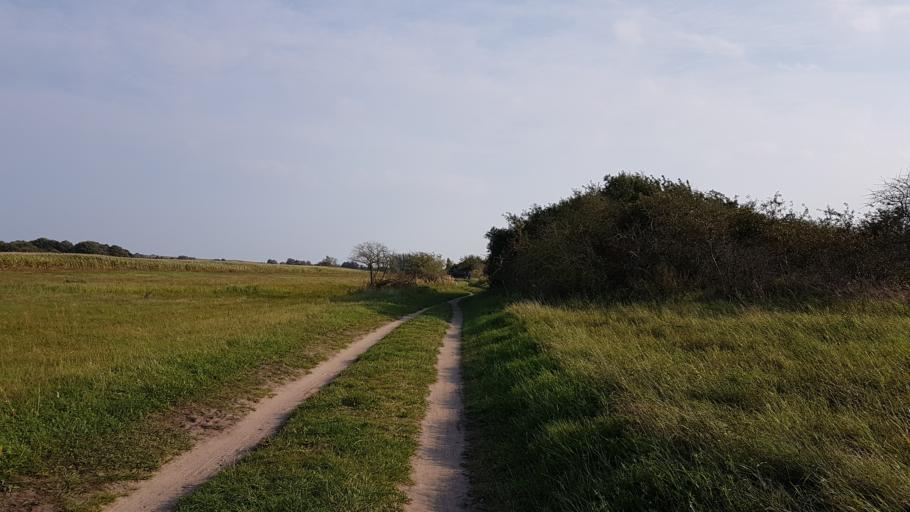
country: DE
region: Mecklenburg-Vorpommern
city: Glowe
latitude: 54.5531
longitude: 13.5000
